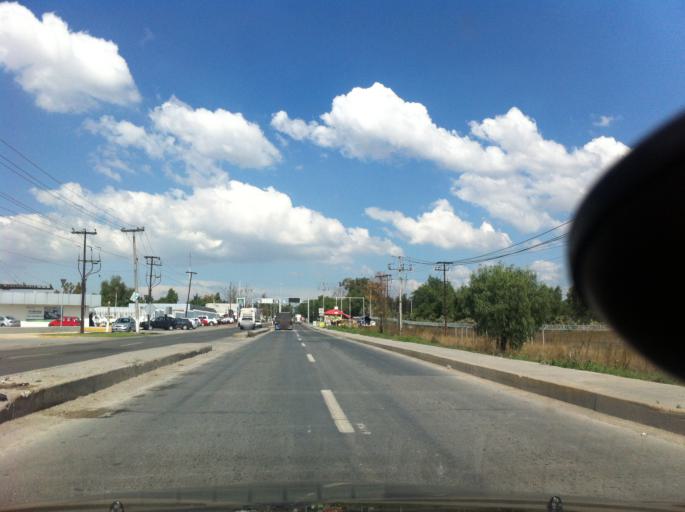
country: MX
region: Mexico
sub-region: Zumpango
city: Zumpango
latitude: 19.8082
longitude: -99.1122
